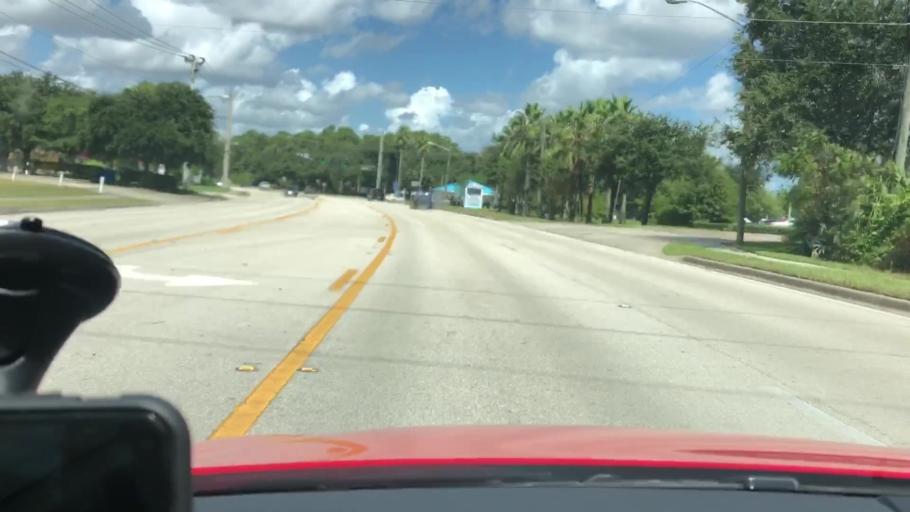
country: US
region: Florida
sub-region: Volusia County
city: Port Orange
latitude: 29.1284
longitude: -81.0254
